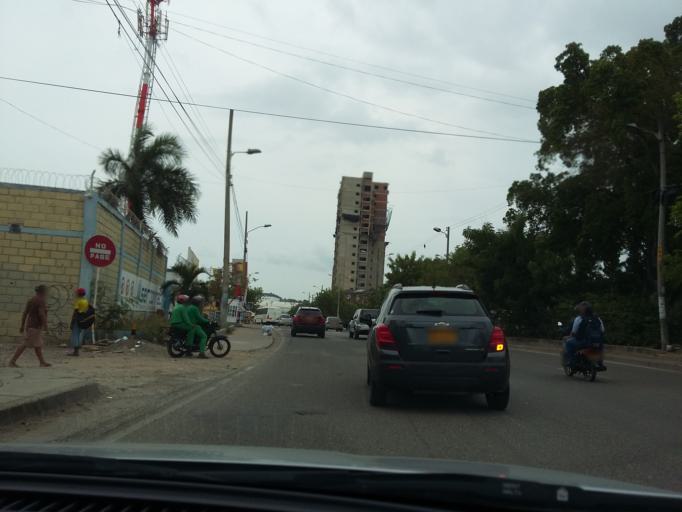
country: CO
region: Bolivar
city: Cartagena
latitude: 10.3857
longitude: -75.5010
